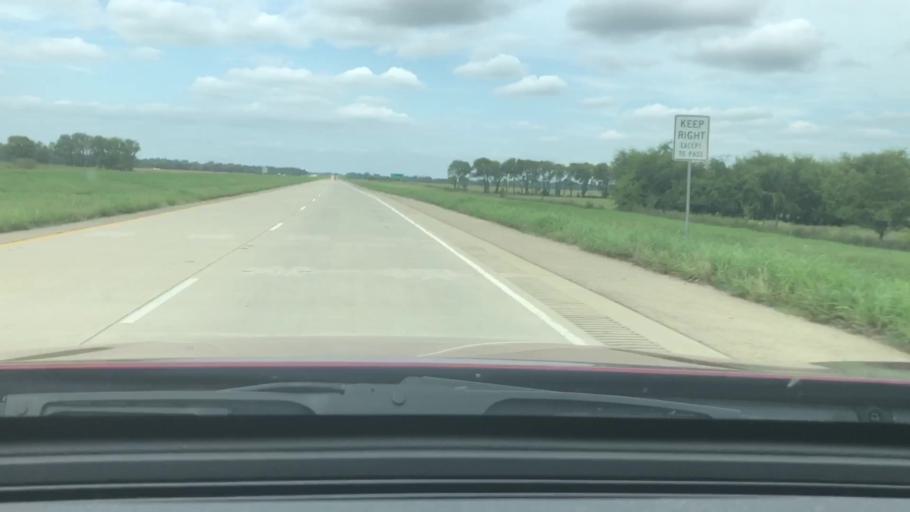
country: US
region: Louisiana
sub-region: Caddo Parish
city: Vivian
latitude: 32.8646
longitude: -93.8614
